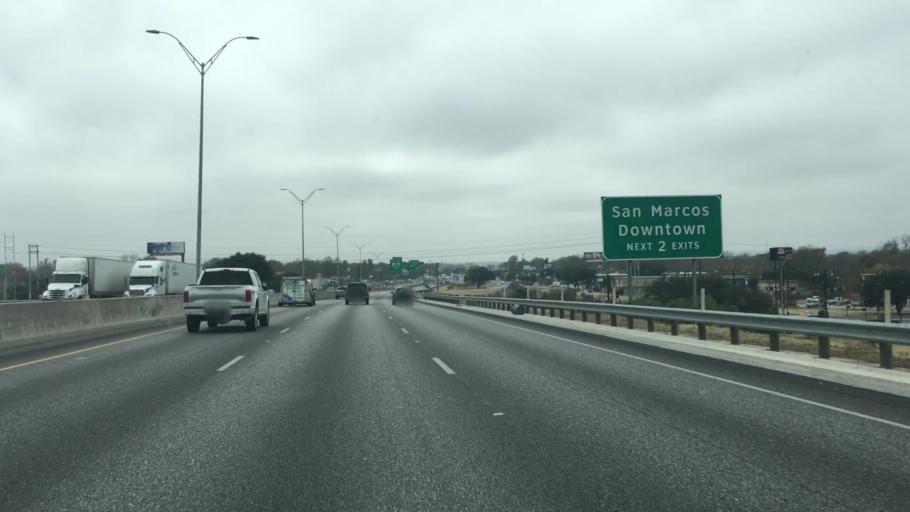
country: US
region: Texas
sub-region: Hays County
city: San Marcos
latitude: 29.8839
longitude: -97.9208
